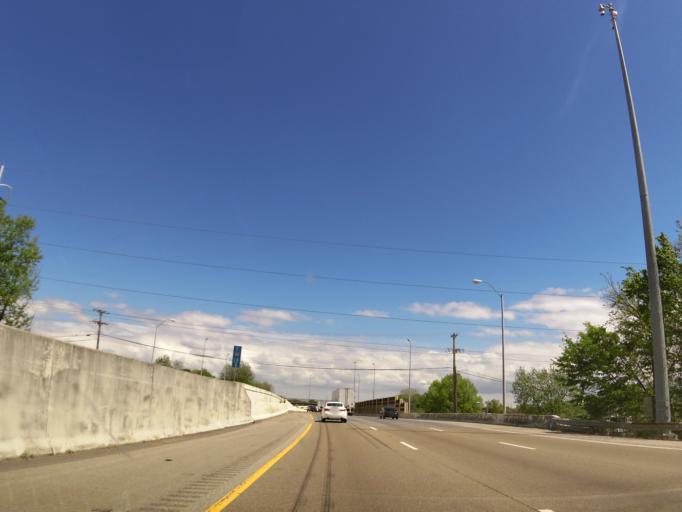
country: US
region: Tennessee
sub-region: Shelby County
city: Memphis
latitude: 35.1501
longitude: -90.0303
